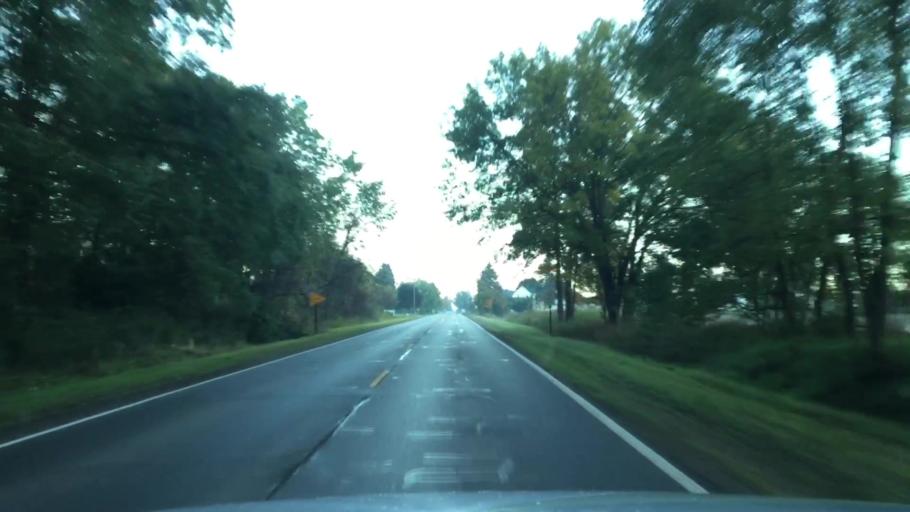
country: US
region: Michigan
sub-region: Livingston County
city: Howell
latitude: 42.6590
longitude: -83.9356
